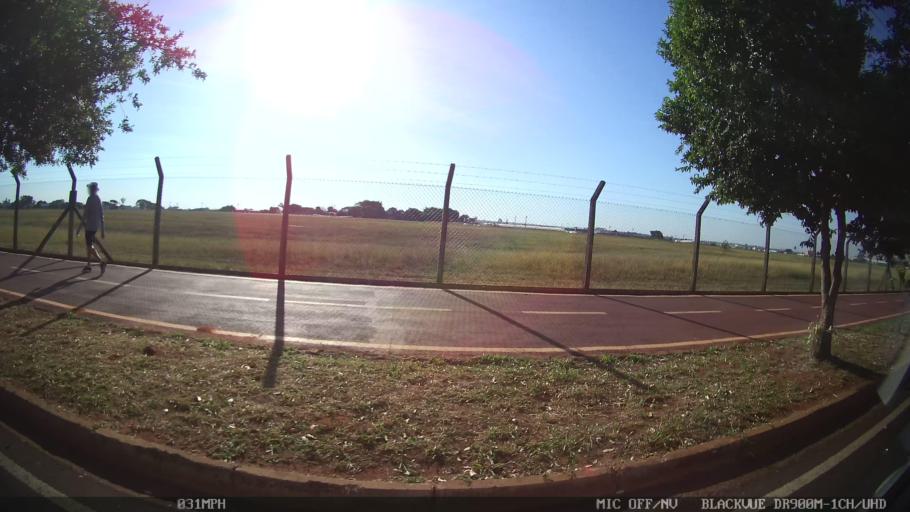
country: BR
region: Sao Paulo
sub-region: Sao Jose Do Rio Preto
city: Sao Jose do Rio Preto
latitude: -20.8164
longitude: -49.4036
